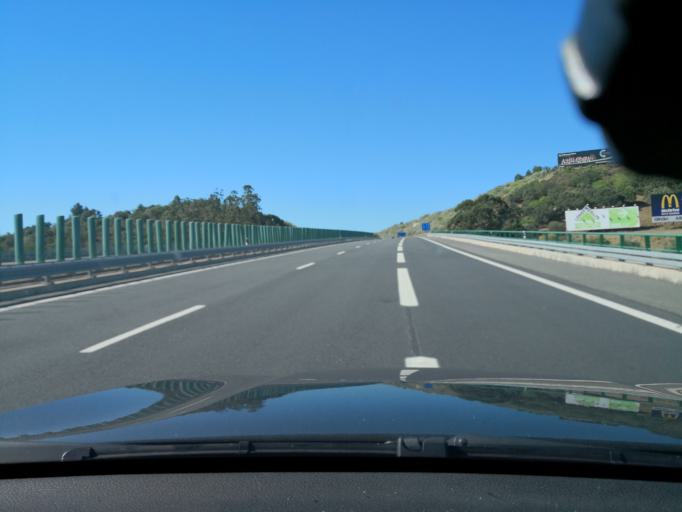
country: PT
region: Faro
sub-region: Silves
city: Sao Bartolomeu de Messines
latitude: 37.2483
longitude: -8.2557
